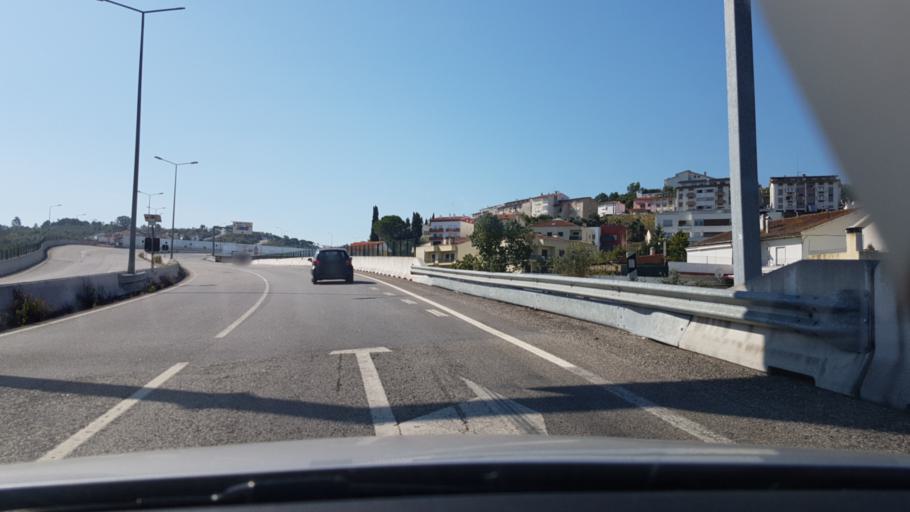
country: PT
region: Coimbra
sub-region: Coimbra
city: Coimbra
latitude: 40.1975
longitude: -8.4528
